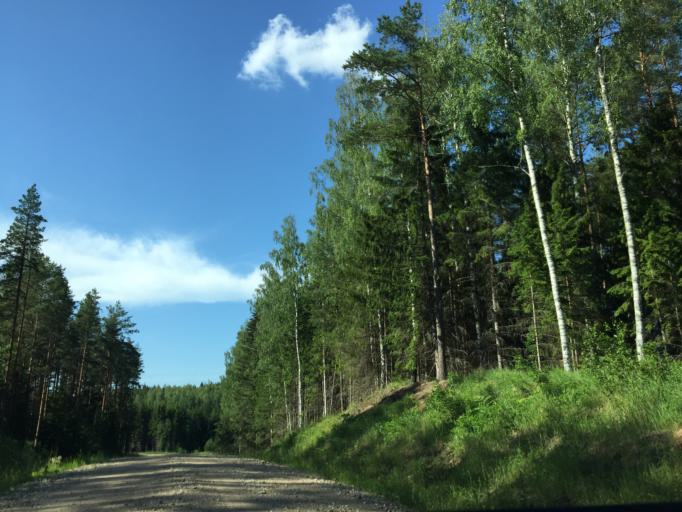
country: LV
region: Tukuma Rajons
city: Tukums
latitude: 57.0219
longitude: 23.2242
